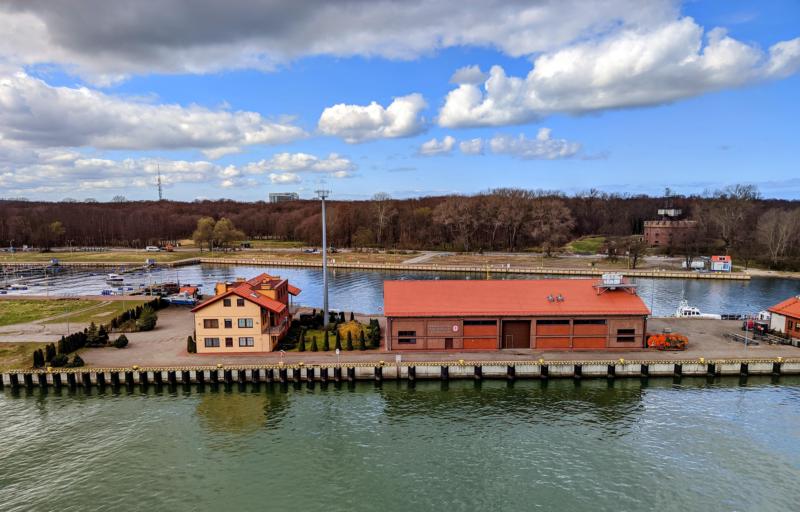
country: PL
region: West Pomeranian Voivodeship
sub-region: Swinoujscie
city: Swinoujscie
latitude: 53.9132
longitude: 14.2770
